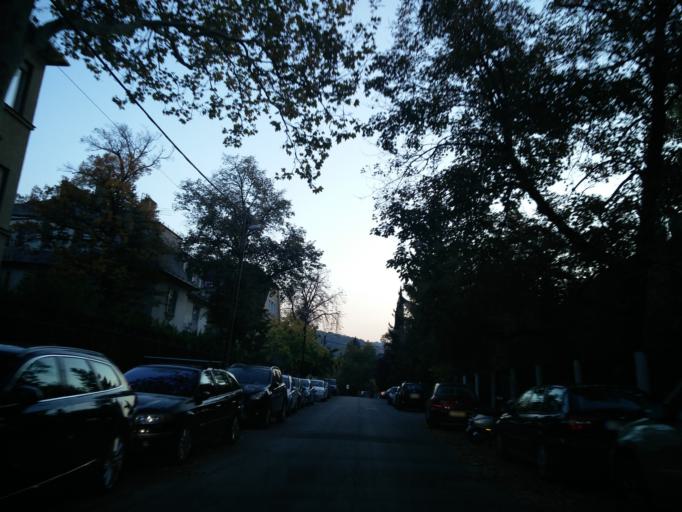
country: HU
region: Budapest
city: Budapest II. keruelet
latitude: 47.5119
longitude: 19.0185
